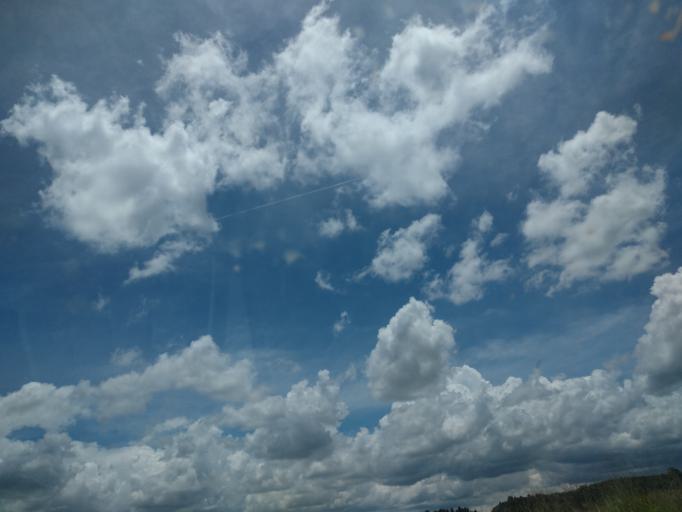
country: BR
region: Minas Gerais
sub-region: Tiradentes
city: Tiradentes
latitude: -20.9093
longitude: -44.2734
